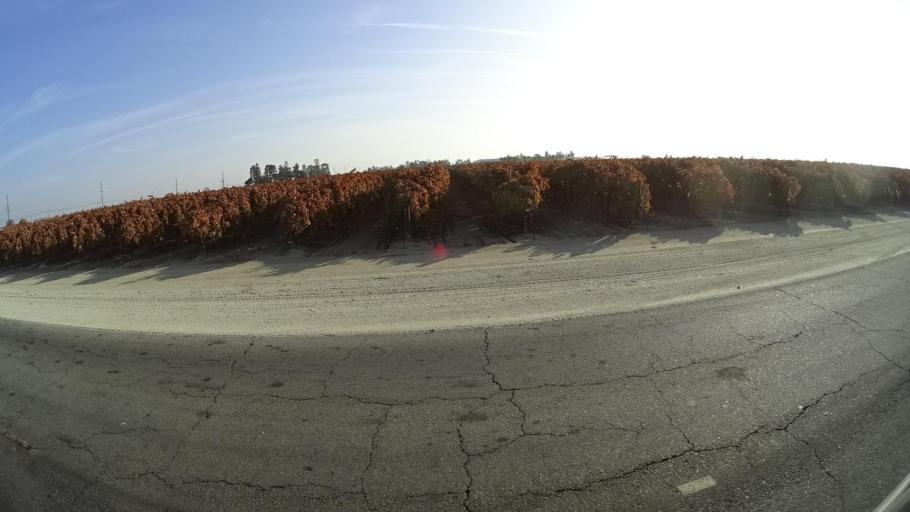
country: US
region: California
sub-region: Kern County
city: Delano
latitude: 35.7743
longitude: -119.1875
